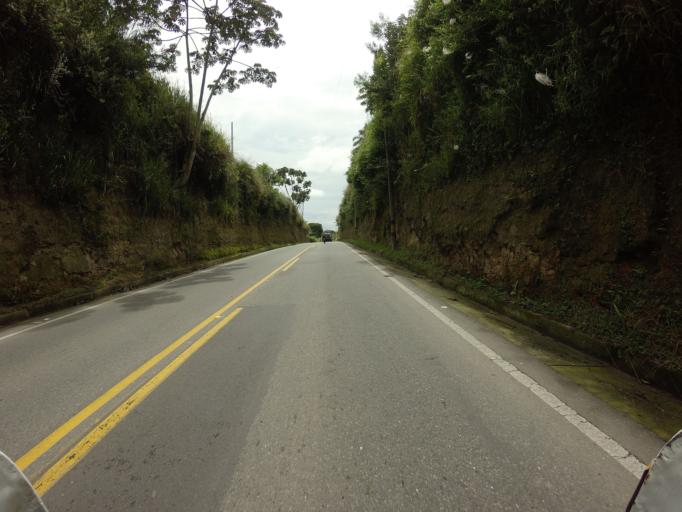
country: CO
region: Quindio
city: Quimbaya
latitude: 4.5980
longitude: -75.7791
